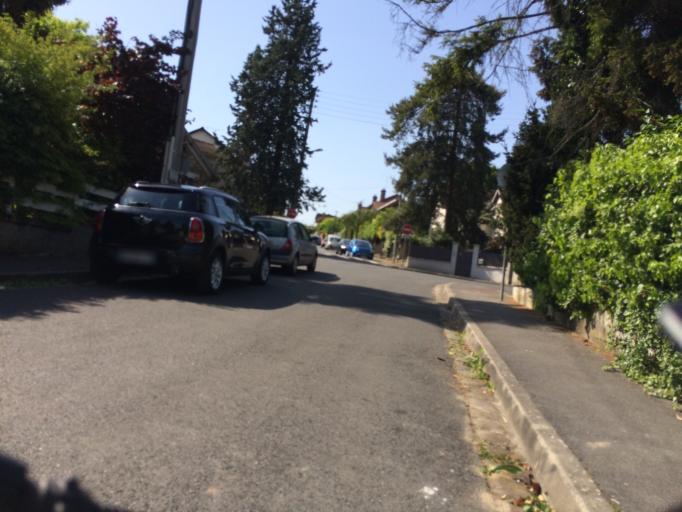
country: FR
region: Ile-de-France
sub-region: Departement de l'Essonne
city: Verrieres-le-Buisson
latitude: 48.7401
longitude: 2.2686
